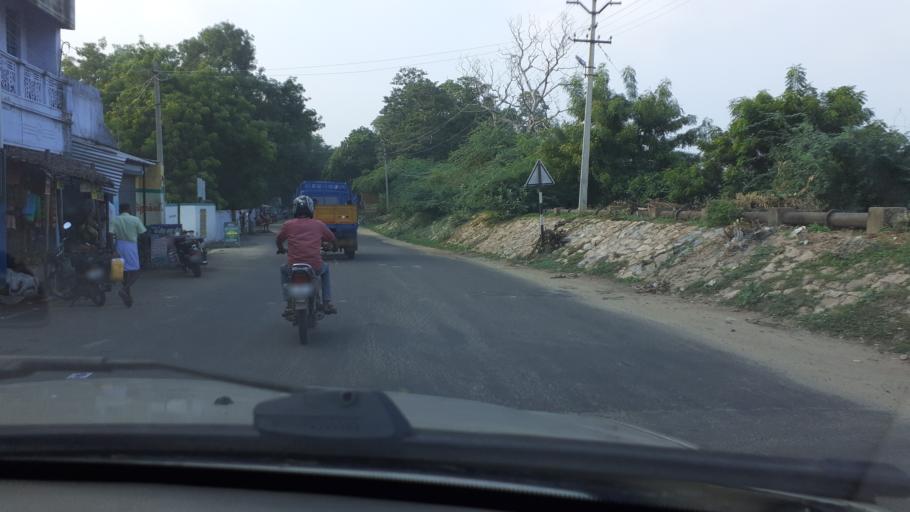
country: IN
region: Tamil Nadu
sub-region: Thoothukkudi
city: Srivaikuntam
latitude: 8.6248
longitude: 77.9089
